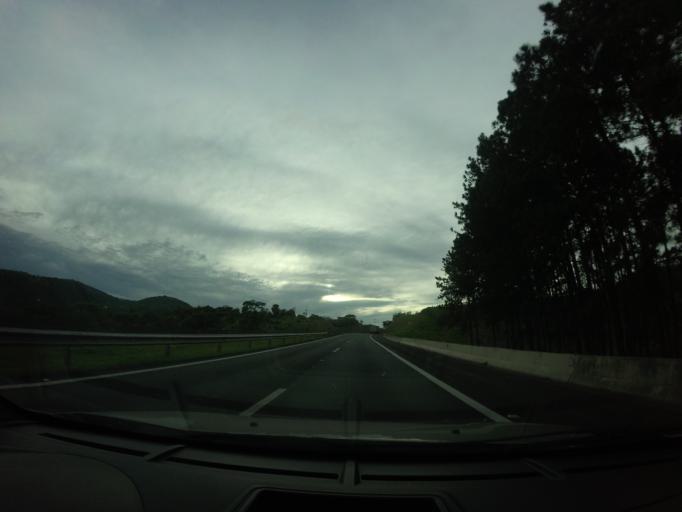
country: BR
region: Sao Paulo
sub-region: Itatiba
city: Itatiba
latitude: -22.9305
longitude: -46.9034
